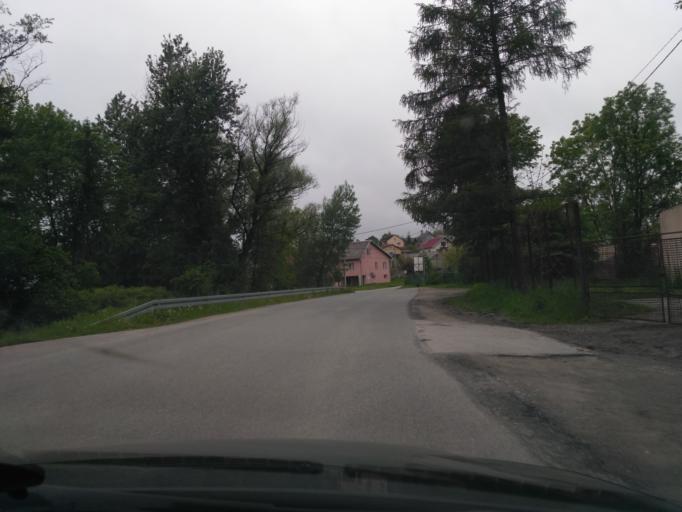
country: PL
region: Subcarpathian Voivodeship
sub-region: Powiat debicki
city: Jodlowa
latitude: 49.8753
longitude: 21.2976
